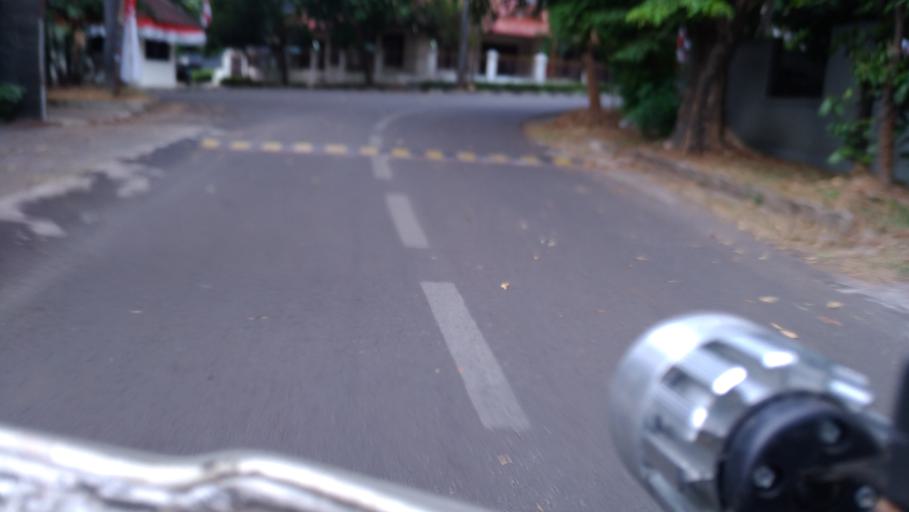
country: ID
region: West Java
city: Depok
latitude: -6.3533
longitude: 106.8868
